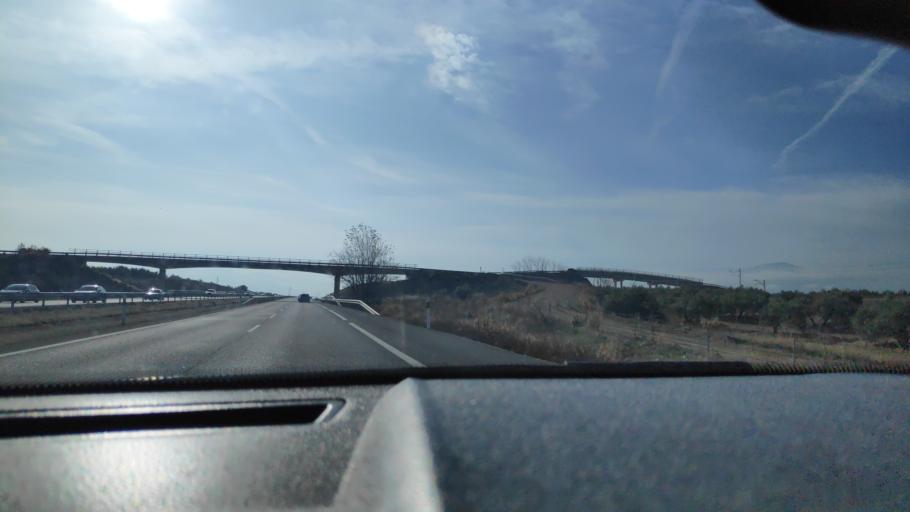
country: ES
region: Andalusia
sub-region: Provincia de Jaen
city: Jaen
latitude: 37.8508
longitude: -3.7649
